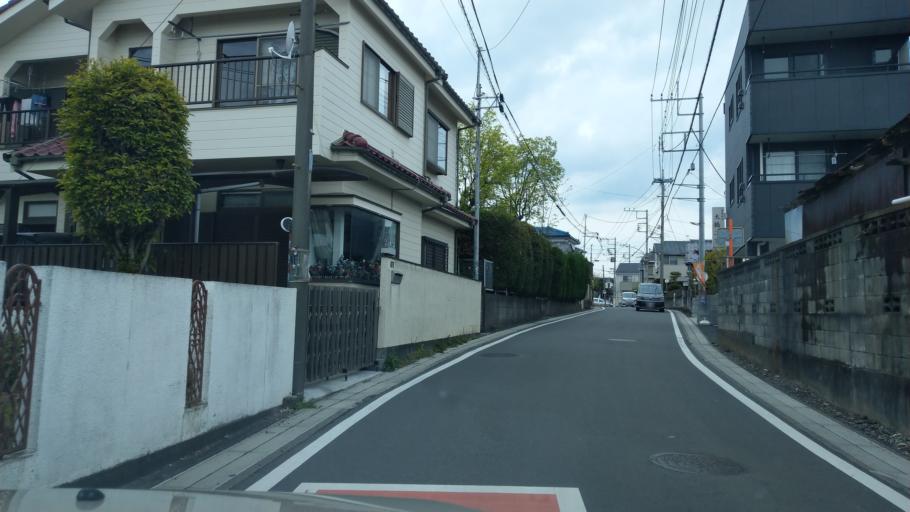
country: JP
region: Saitama
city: Yono
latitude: 35.9022
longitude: 139.5952
